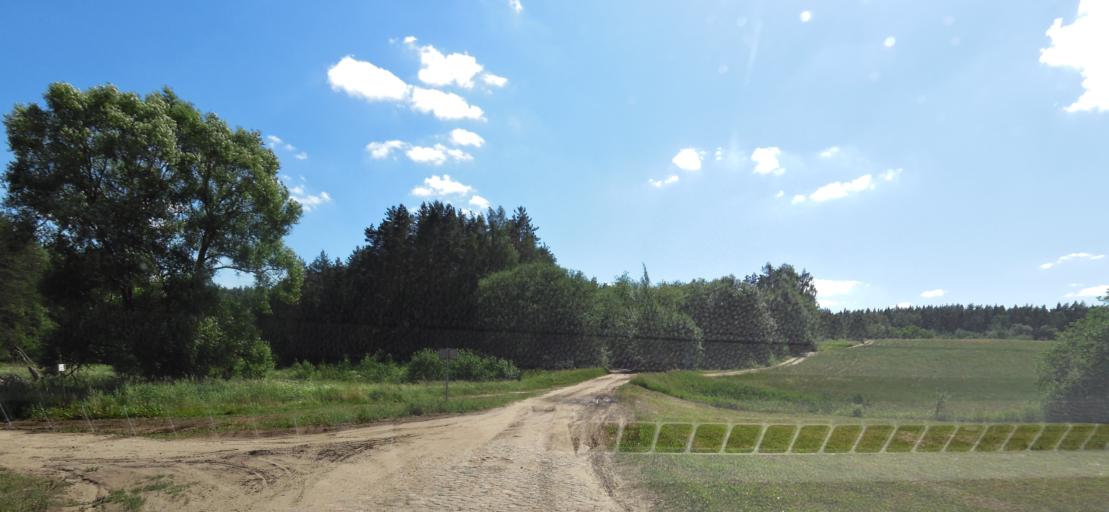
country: LT
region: Vilnius County
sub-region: Vilnius
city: Fabijoniskes
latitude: 54.8305
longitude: 25.3241
